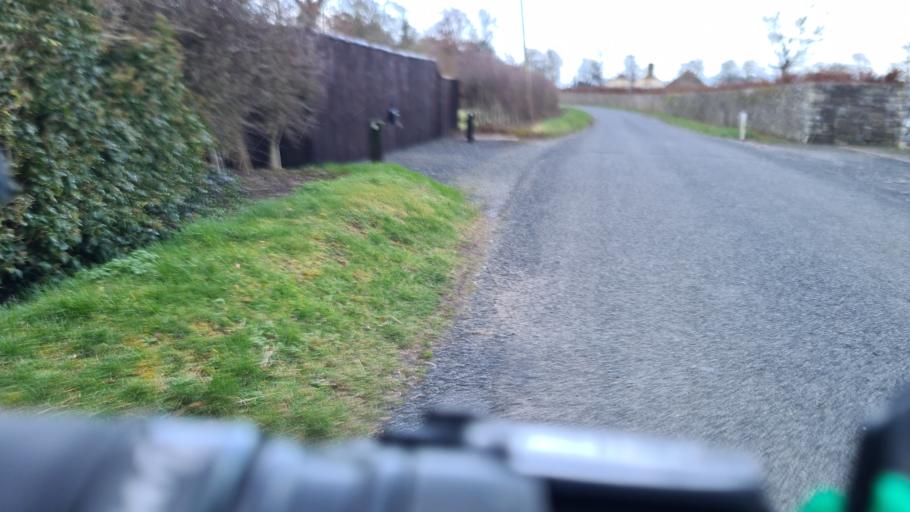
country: IE
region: Leinster
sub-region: Kildare
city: Maynooth
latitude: 53.3388
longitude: -6.5911
